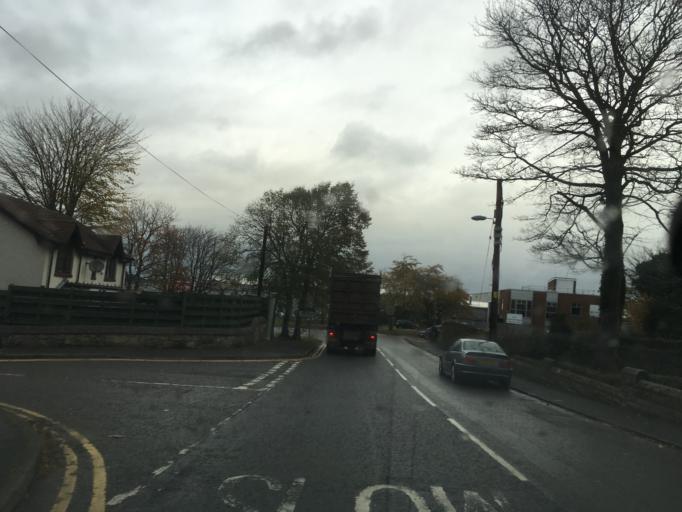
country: GB
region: Scotland
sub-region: Falkirk
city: Bo'ness
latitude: 56.0143
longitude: -3.5757
